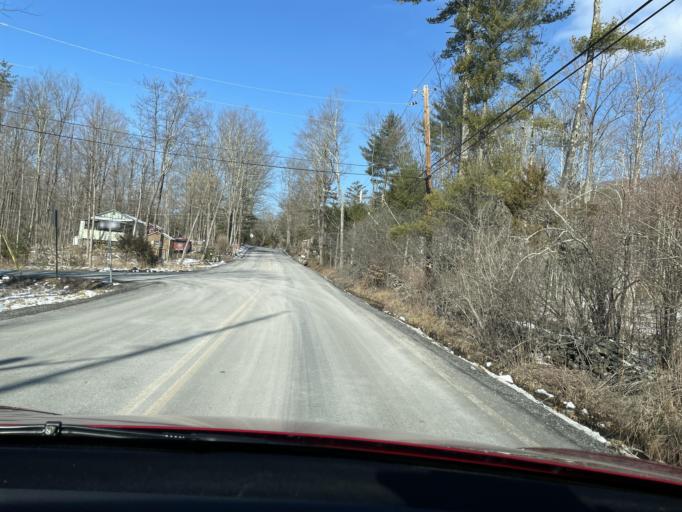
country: US
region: New York
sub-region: Ulster County
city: Woodstock
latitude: 42.0507
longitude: -74.1377
